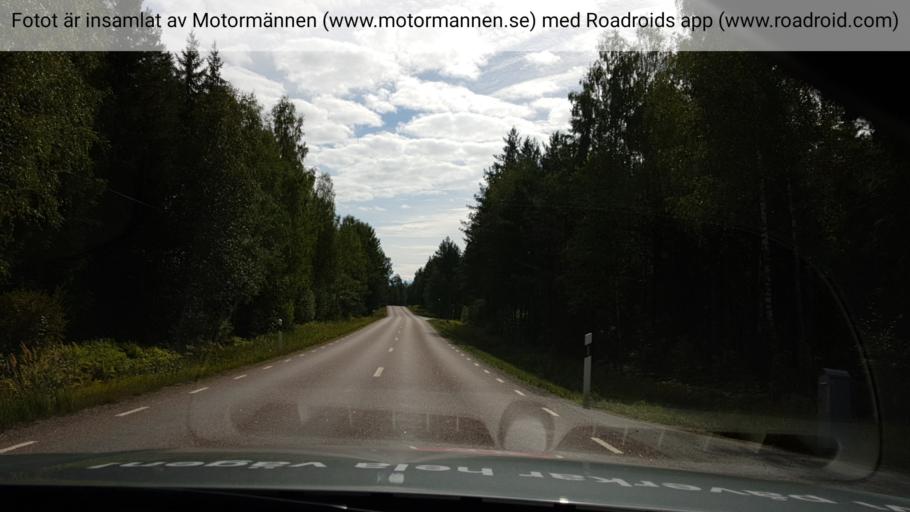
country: SE
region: Uppsala
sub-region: Heby Kommun
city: OEstervala
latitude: 60.0372
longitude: 17.2518
